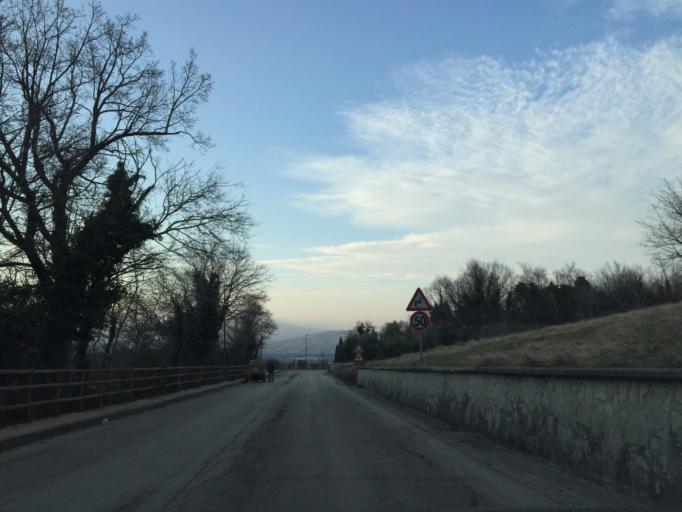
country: IT
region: Molise
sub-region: Provincia di Campobasso
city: Guardiaregia
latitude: 41.4390
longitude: 14.5463
